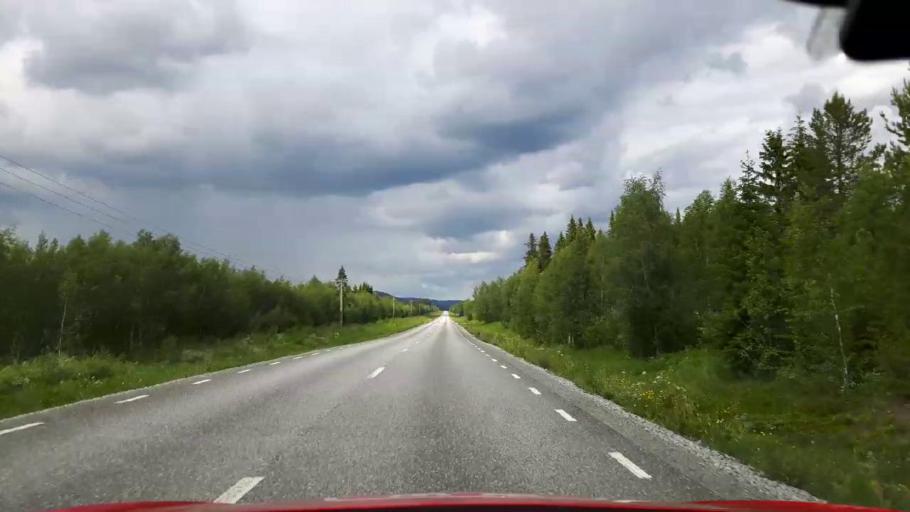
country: SE
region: Jaemtland
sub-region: Krokoms Kommun
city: Krokom
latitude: 63.6539
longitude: 14.3706
